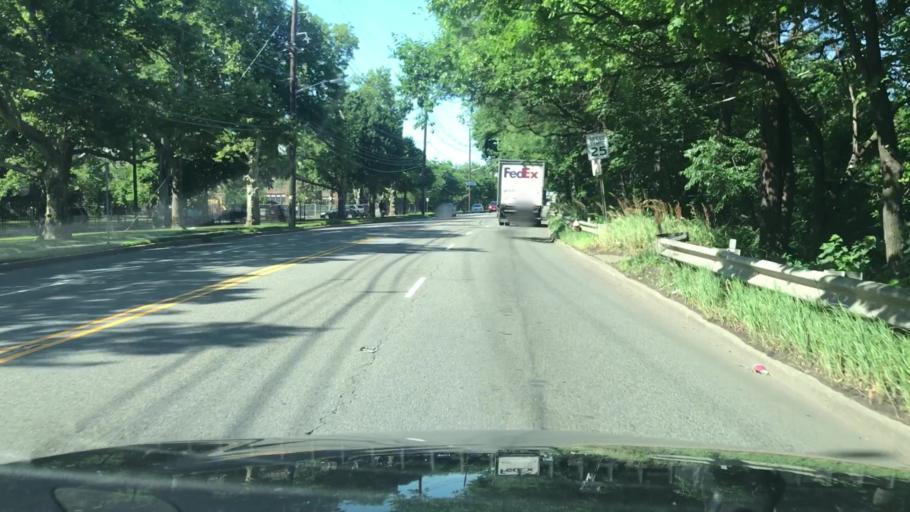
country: US
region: New Jersey
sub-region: Hudson County
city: Secaucus
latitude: 40.7817
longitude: -74.0579
